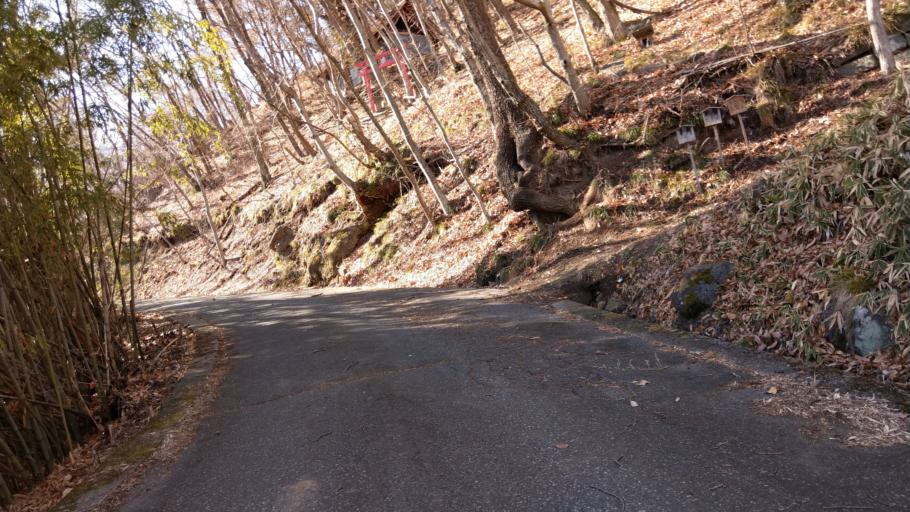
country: JP
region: Nagano
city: Komoro
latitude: 36.3021
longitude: 138.4166
